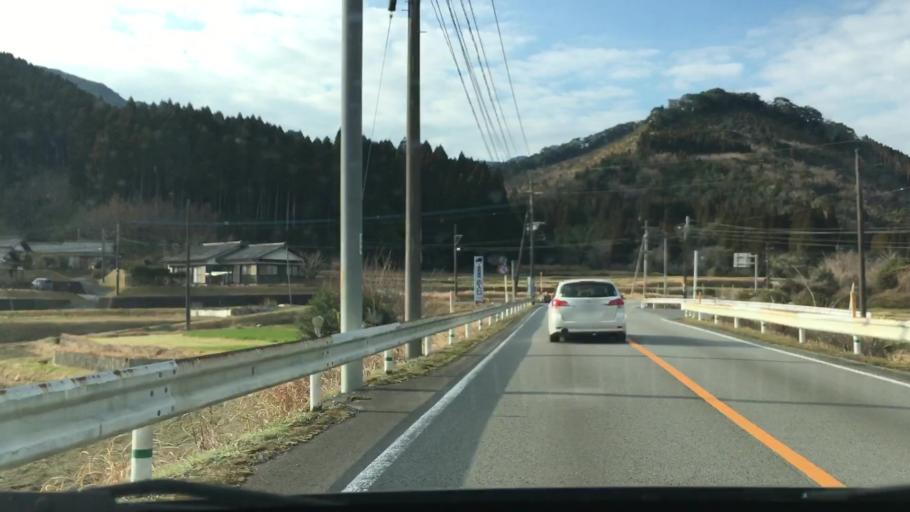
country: JP
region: Miyazaki
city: Nichinan
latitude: 31.7448
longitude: 131.3369
